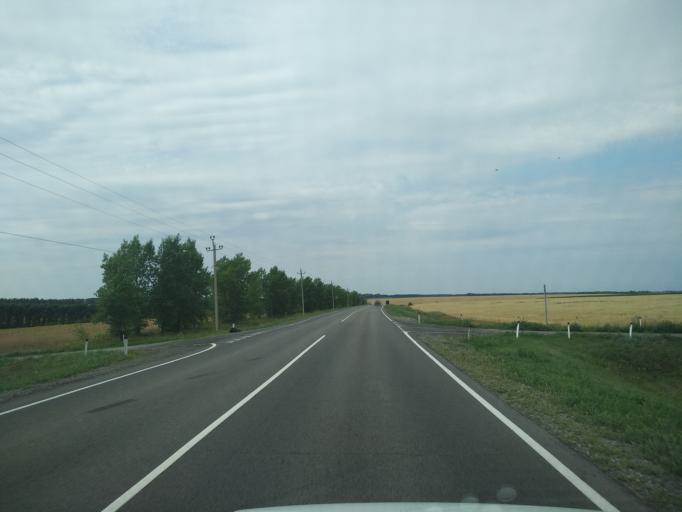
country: RU
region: Voronezj
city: Pereleshinskiy
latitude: 51.8244
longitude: 40.2769
